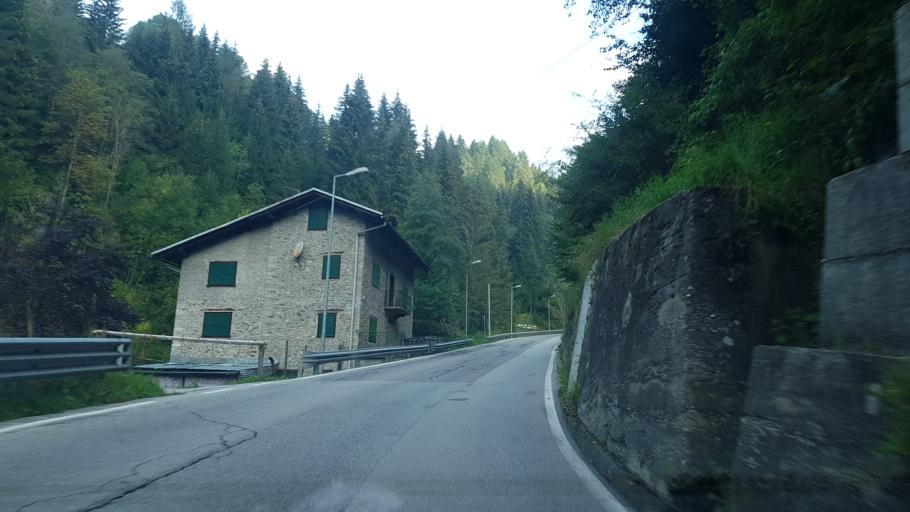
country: IT
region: Veneto
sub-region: Provincia di Belluno
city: San Pietro di Cadore
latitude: 46.5706
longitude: 12.5846
